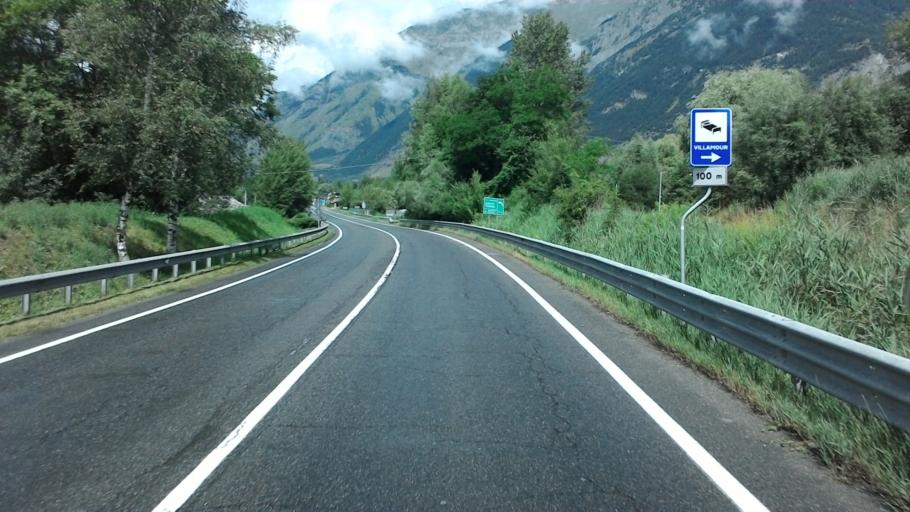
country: IT
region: Aosta Valley
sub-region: Valle d'Aosta
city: La Salle
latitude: 45.7468
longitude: 7.0593
